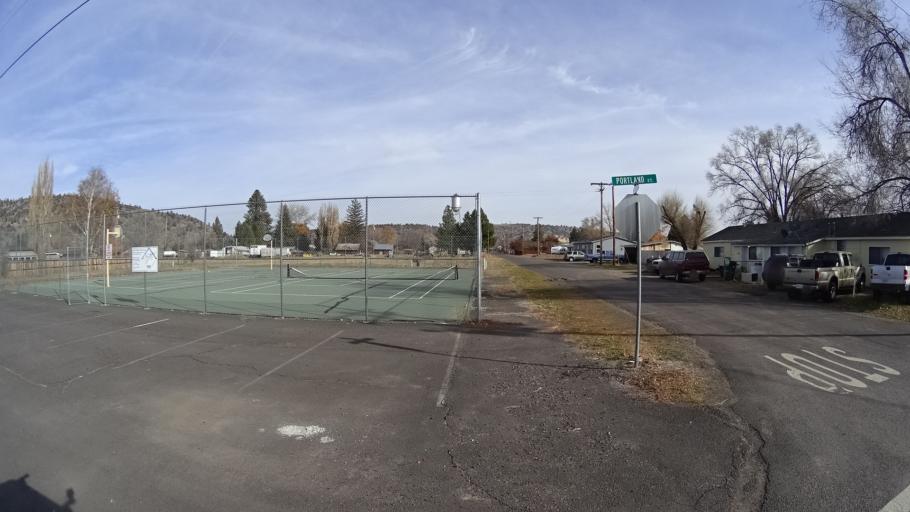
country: US
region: Oregon
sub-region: Klamath County
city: Klamath Falls
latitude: 41.9658
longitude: -121.9240
